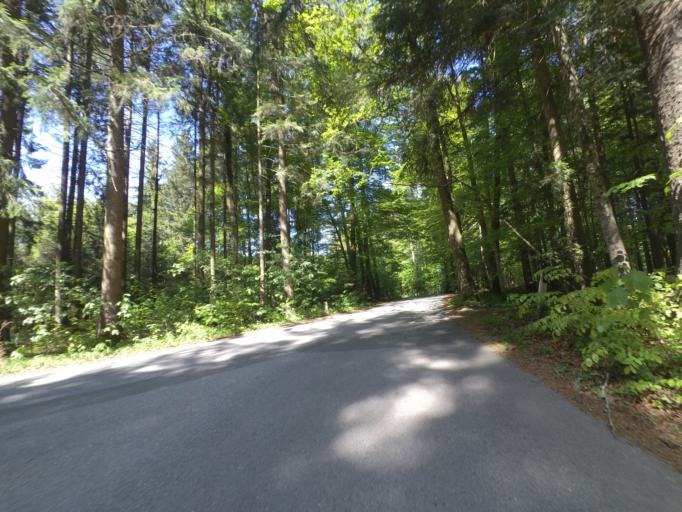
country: AT
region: Salzburg
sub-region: Politischer Bezirk Salzburg-Umgebung
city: Schleedorf
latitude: 47.9357
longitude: 13.1304
